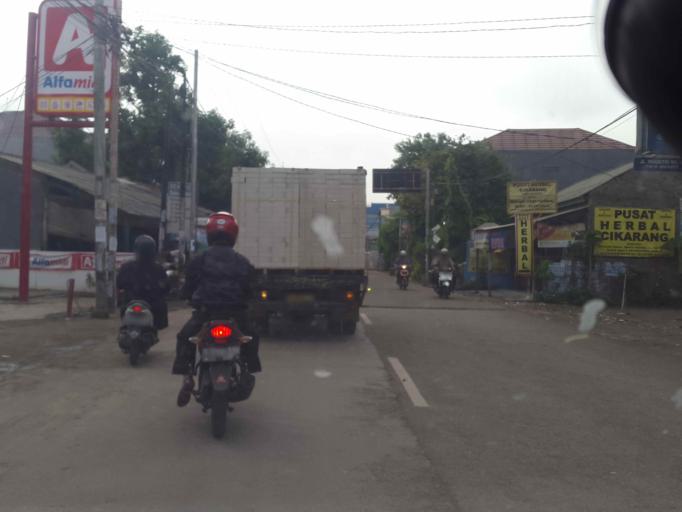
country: ID
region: West Java
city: Cikarang
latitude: -6.2600
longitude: 107.1471
